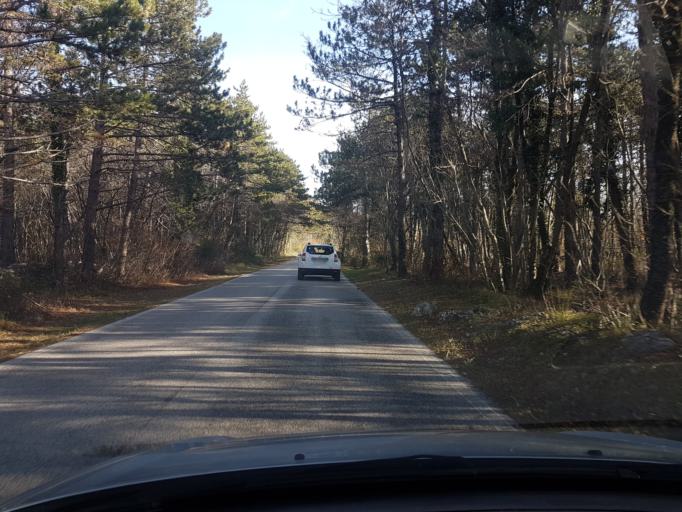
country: IT
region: Friuli Venezia Giulia
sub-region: Provincia di Trieste
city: Aurisina
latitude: 45.7693
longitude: 13.6888
